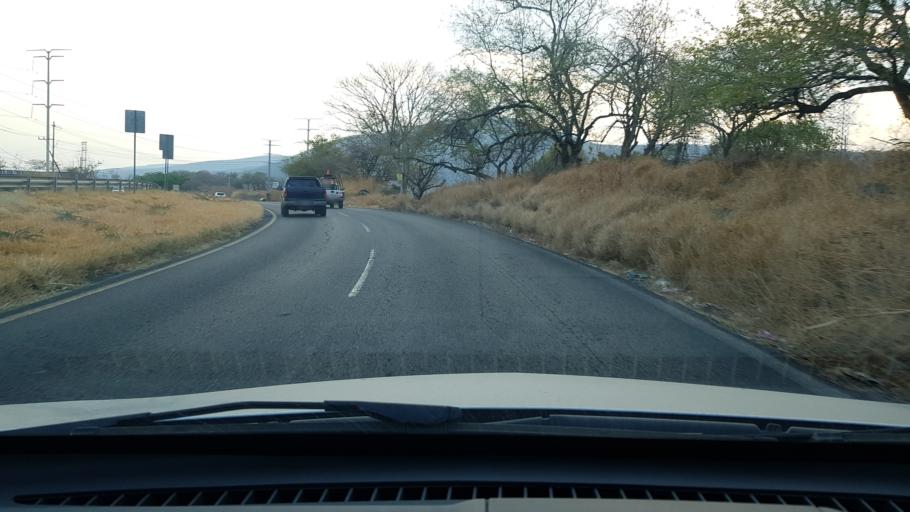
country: MX
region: Morelos
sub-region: Jiutepec
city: Independencia
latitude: 18.8637
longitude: -99.0951
